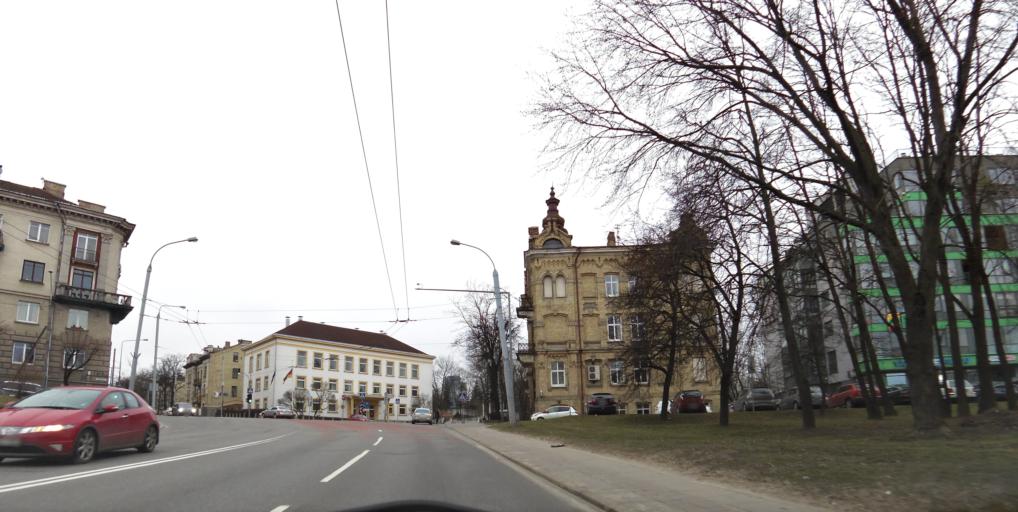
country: LT
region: Vilnius County
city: Naujamiestis
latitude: 54.6847
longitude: 25.2651
